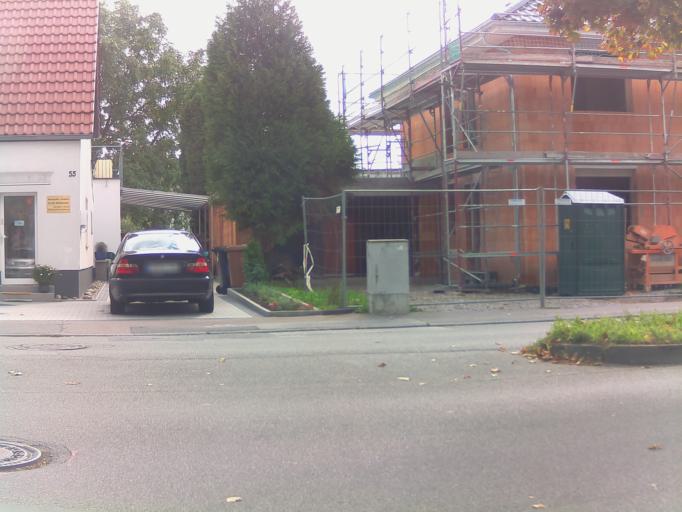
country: DE
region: Baden-Wuerttemberg
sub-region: Karlsruhe Region
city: Weinheim
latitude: 49.5455
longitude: 8.6409
